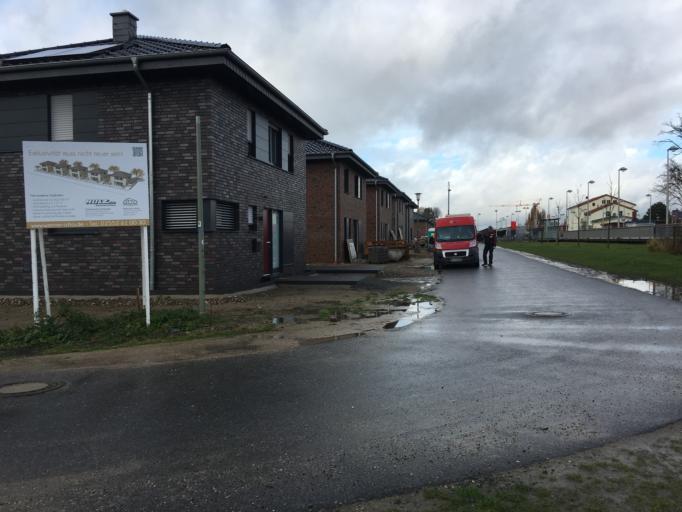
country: DE
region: North Rhine-Westphalia
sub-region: Regierungsbezirk Munster
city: Steinfurt
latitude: 52.1460
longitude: 7.3307
